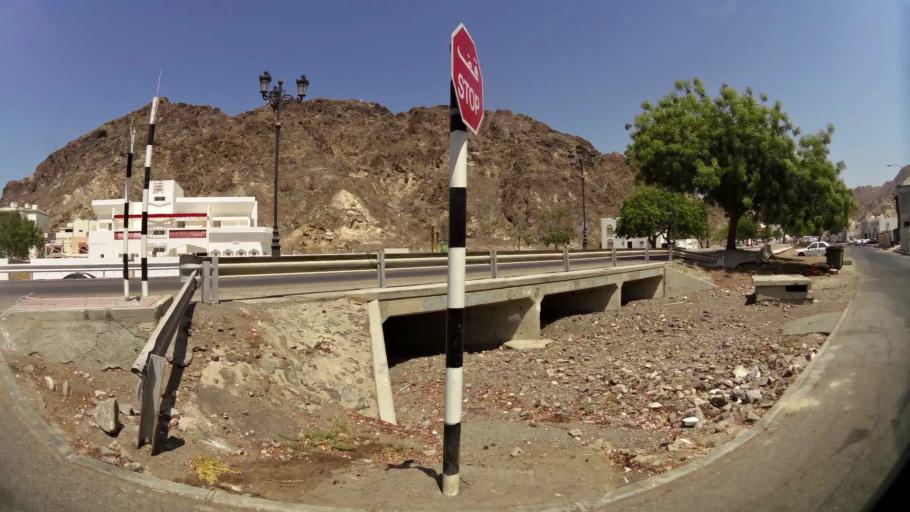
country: OM
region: Muhafazat Masqat
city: Muscat
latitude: 23.5954
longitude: 58.5976
